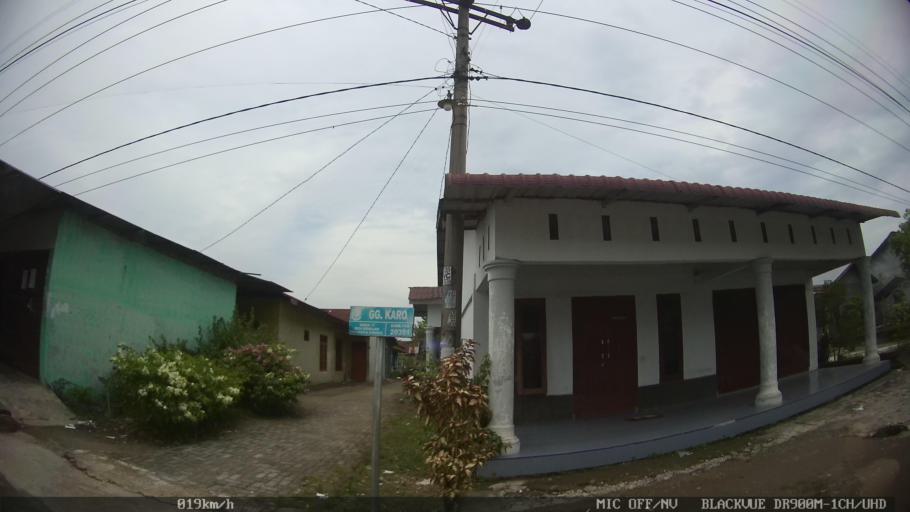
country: ID
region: North Sumatra
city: Sunggal
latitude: 3.6085
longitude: 98.5539
